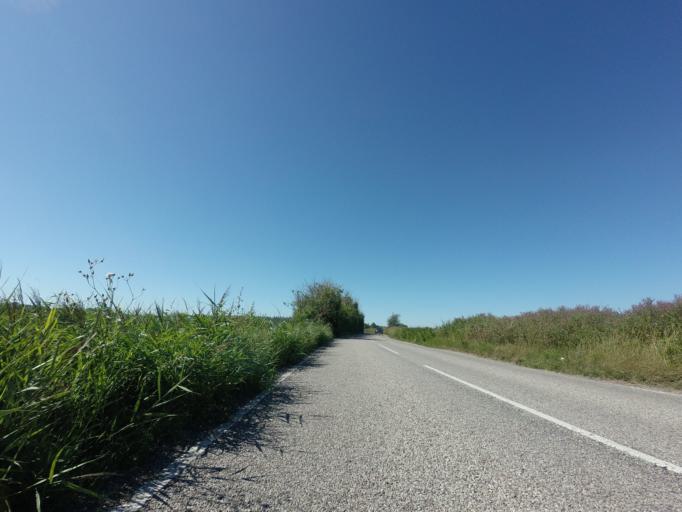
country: GB
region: England
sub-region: Kent
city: Ash
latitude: 51.3172
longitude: 1.2137
